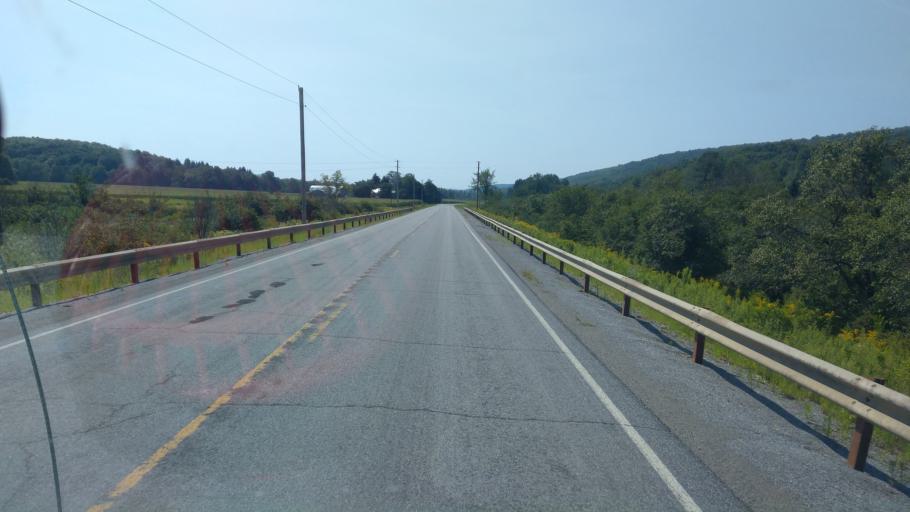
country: US
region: New York
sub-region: Allegany County
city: Alfred
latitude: 42.3549
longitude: -77.9192
